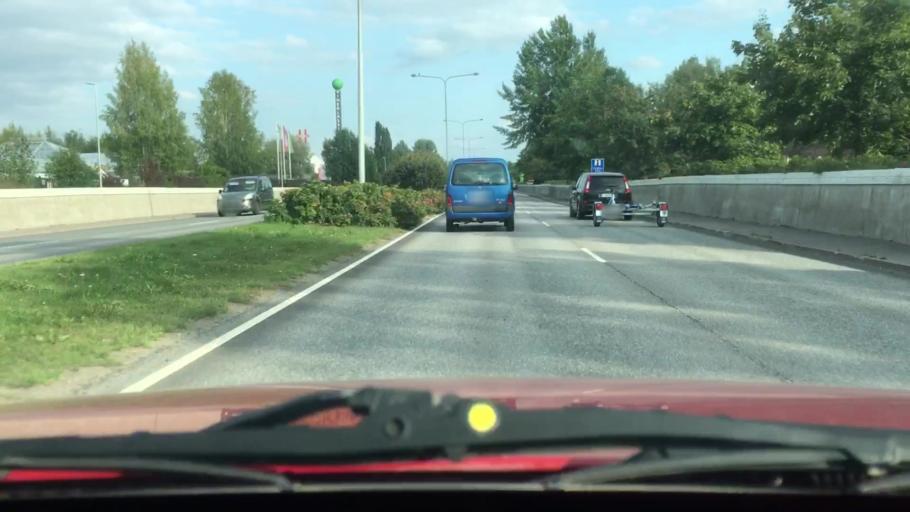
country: FI
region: Varsinais-Suomi
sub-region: Turku
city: Turku
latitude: 60.4581
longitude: 22.2221
